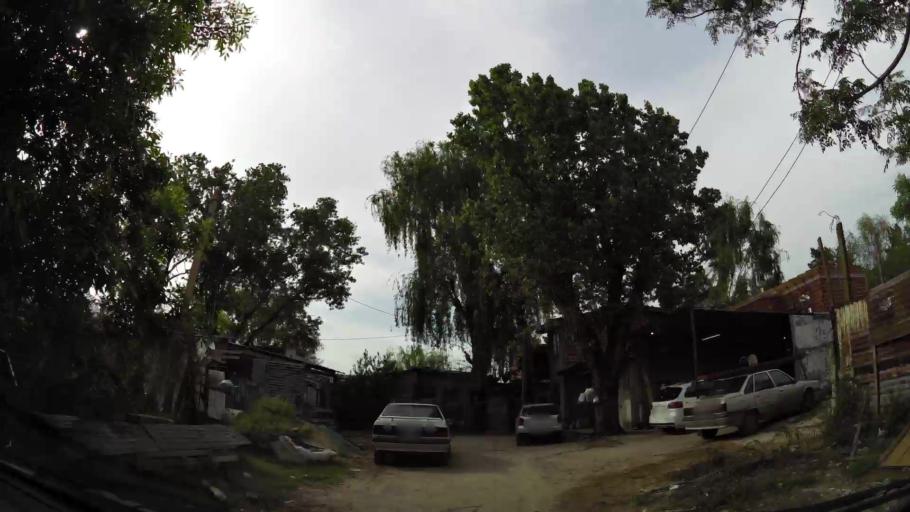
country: AR
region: Buenos Aires
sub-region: Partido de Quilmes
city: Quilmes
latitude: -34.7148
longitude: -58.2398
